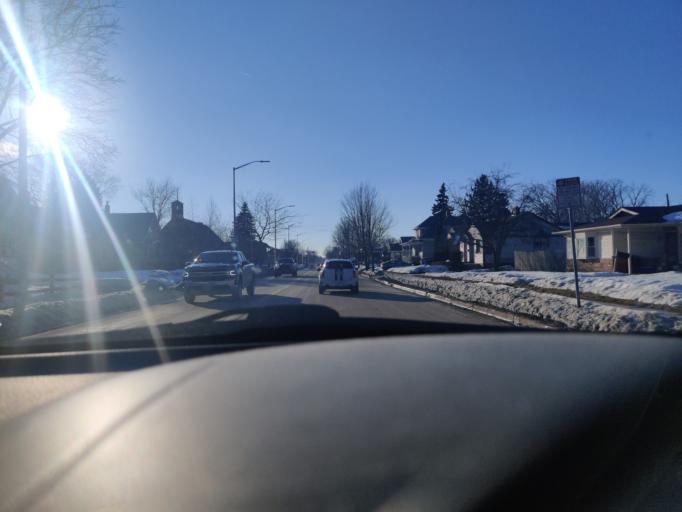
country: US
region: Wisconsin
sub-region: Kenosha County
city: Kenosha
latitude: 42.5659
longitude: -87.8376
